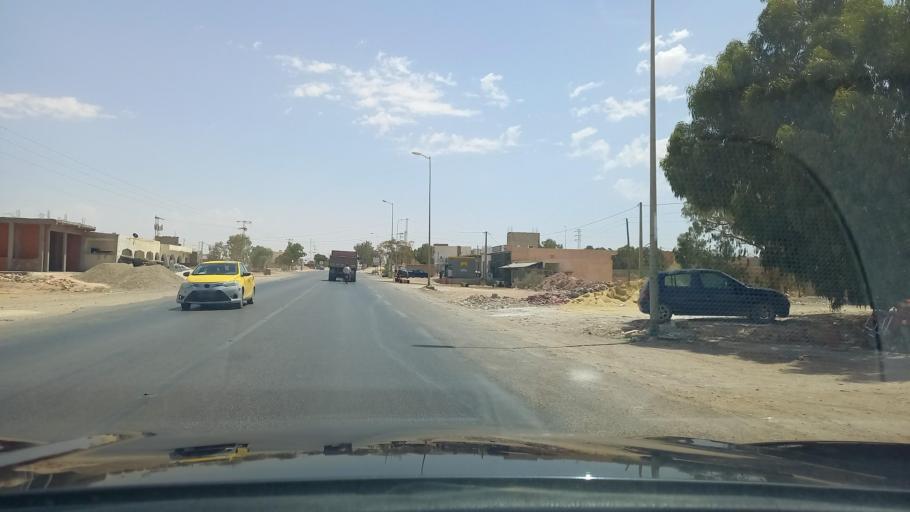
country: TN
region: Madanin
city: Medenine
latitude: 33.3737
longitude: 10.4463
